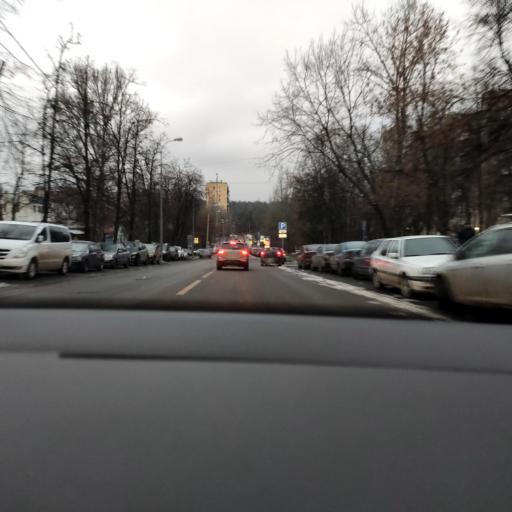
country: RU
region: Moscow
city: Metrogorodok
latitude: 55.8183
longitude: 37.7931
